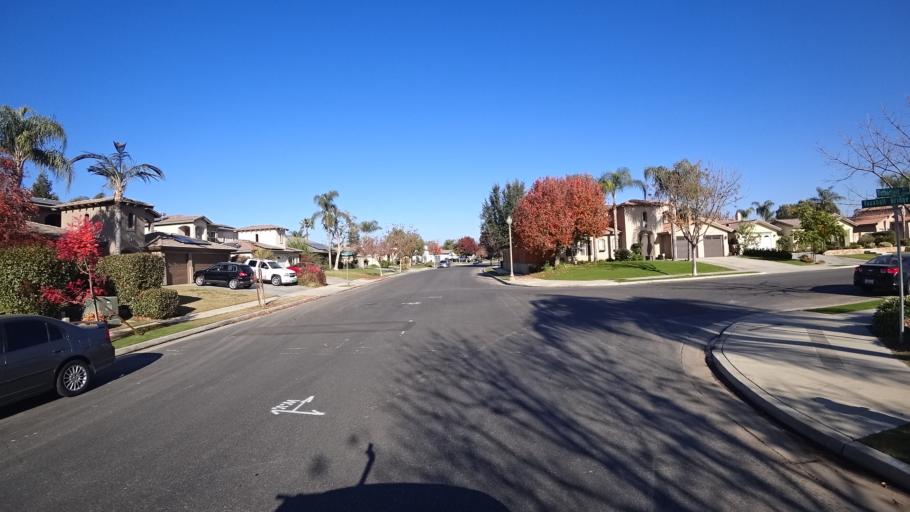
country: US
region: California
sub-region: Kern County
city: Rosedale
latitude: 35.3287
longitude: -119.1300
